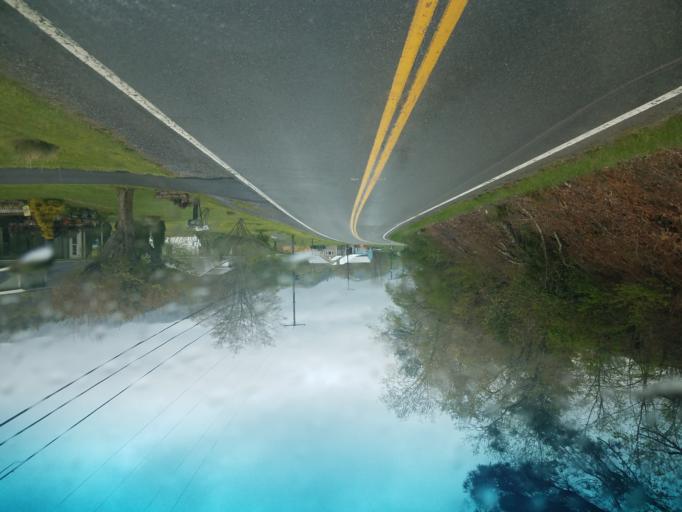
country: US
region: Virginia
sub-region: Bland County
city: Bland
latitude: 37.1619
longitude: -81.1484
